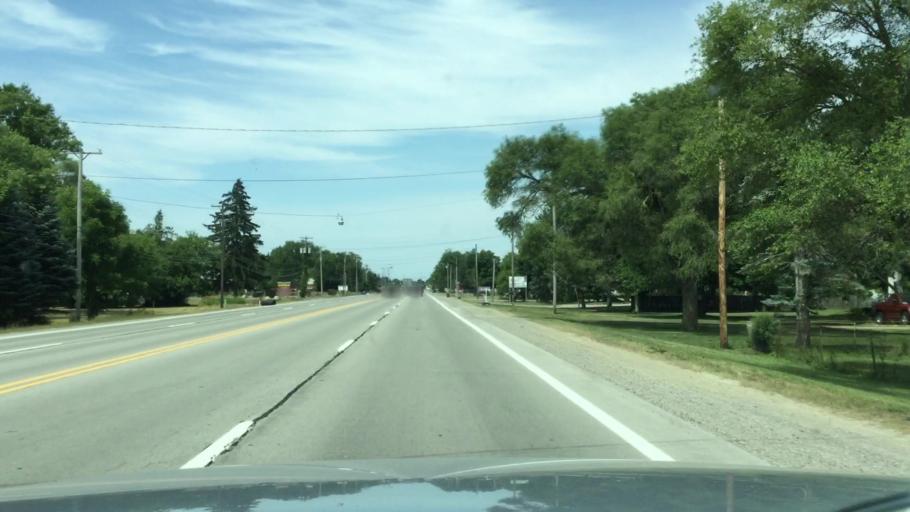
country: US
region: Michigan
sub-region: Genesee County
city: Swartz Creek
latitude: 43.0016
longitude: -83.8020
